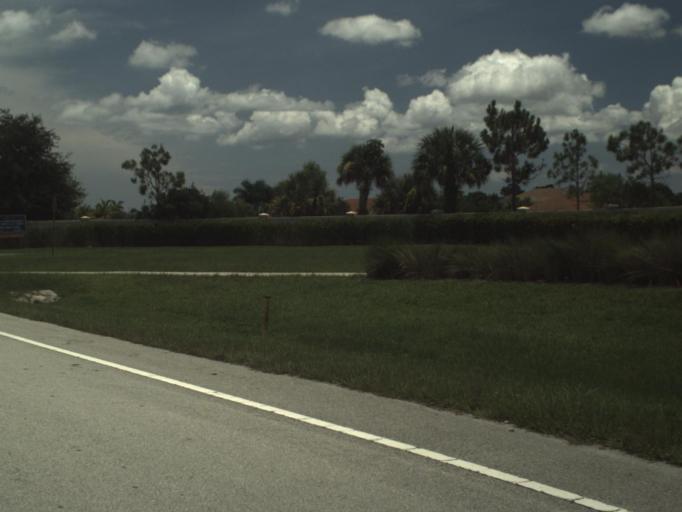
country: US
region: Florida
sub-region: Martin County
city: Palm City
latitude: 27.1160
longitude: -80.2521
